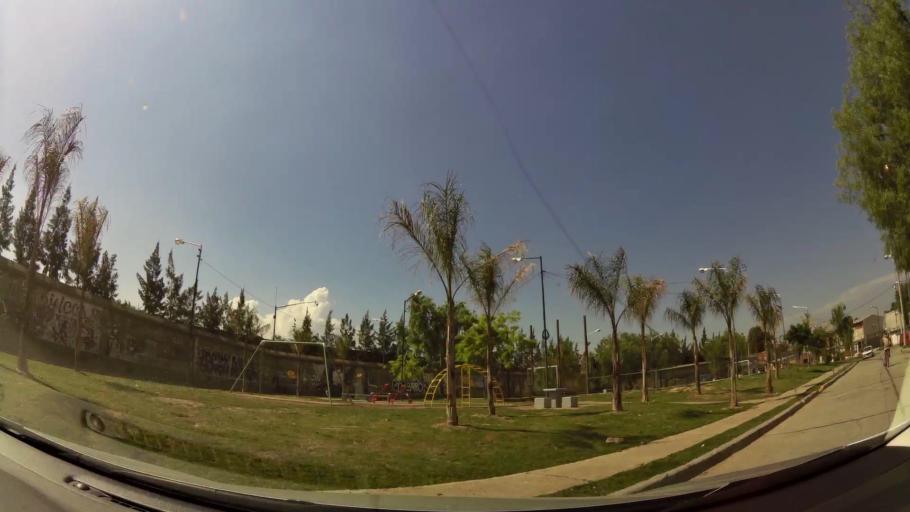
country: AR
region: Buenos Aires
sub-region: Partido de Tigre
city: Tigre
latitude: -34.4655
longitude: -58.5973
